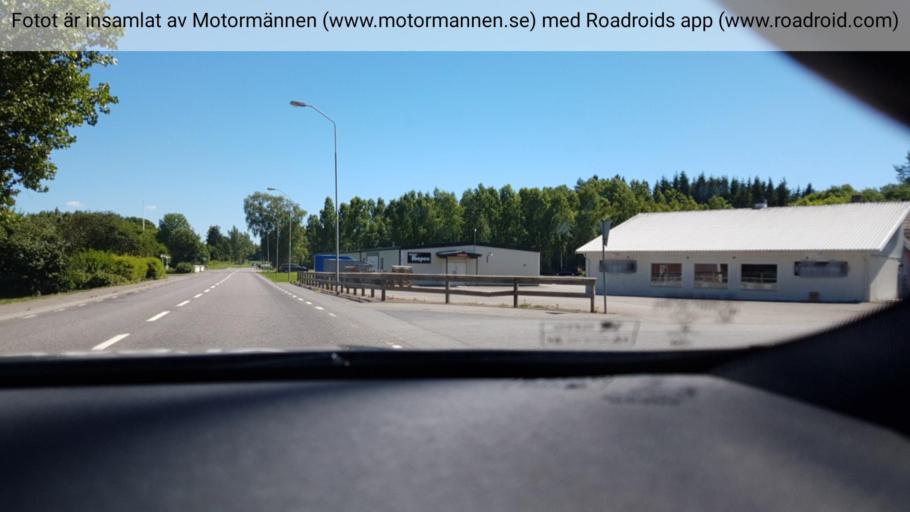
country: SE
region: Vaestra Goetaland
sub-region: Falkopings Kommun
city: Falkoeping
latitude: 58.0718
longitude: 13.5223
